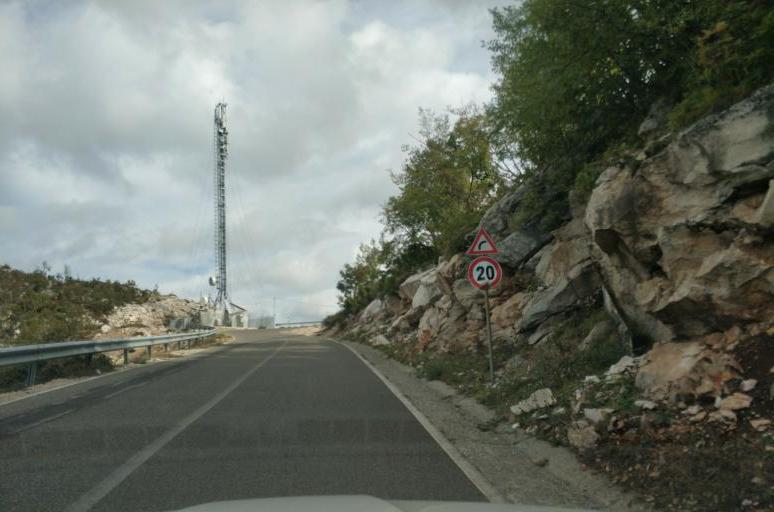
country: AL
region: Durres
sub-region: Rrethi i Krujes
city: Kruje
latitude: 41.5247
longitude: 19.8078
